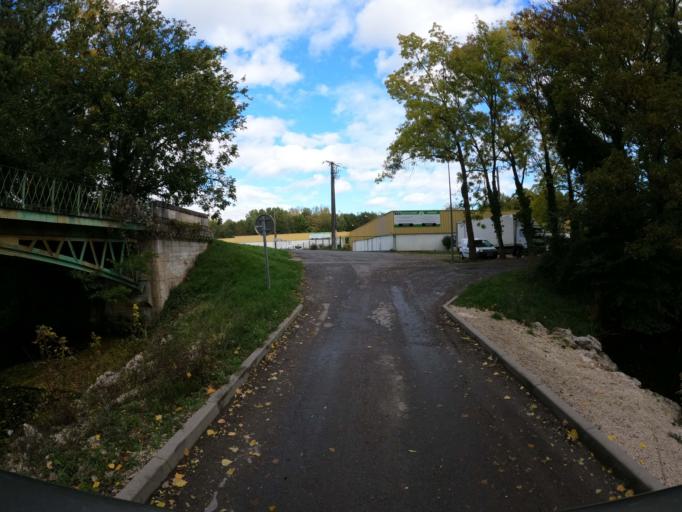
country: FR
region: Ile-de-France
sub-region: Departement de Seine-et-Marne
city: Montry
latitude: 48.8899
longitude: 2.8344
